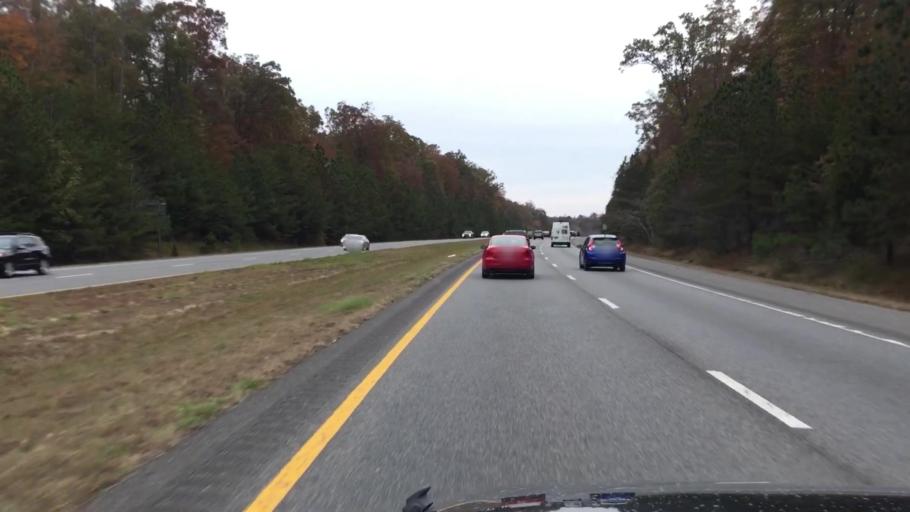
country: US
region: Virginia
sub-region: James City County
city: Williamsburg
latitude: 37.2815
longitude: -76.7534
